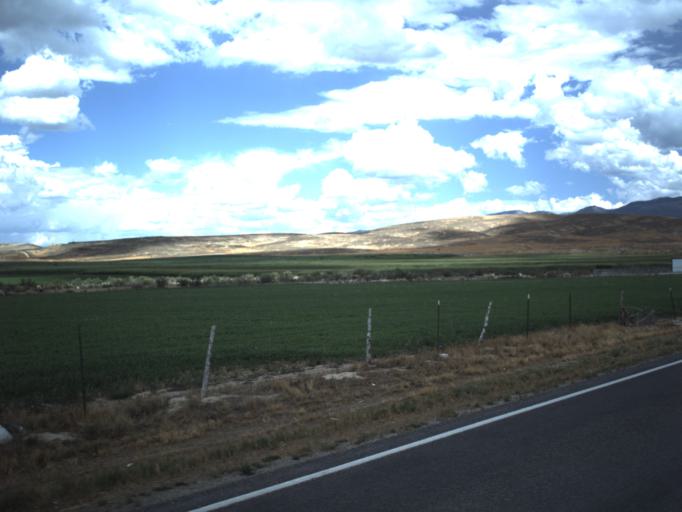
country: US
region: Utah
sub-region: Sanpete County
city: Gunnison
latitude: 39.1417
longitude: -111.7982
